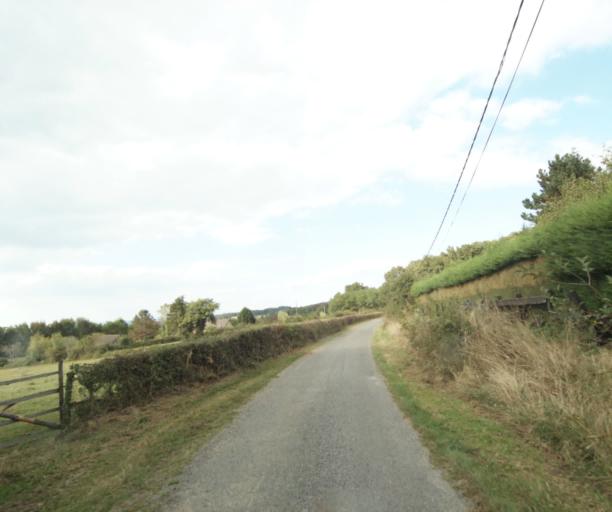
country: FR
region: Bourgogne
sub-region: Departement de Saone-et-Loire
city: Palinges
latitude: 46.5237
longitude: 4.2916
